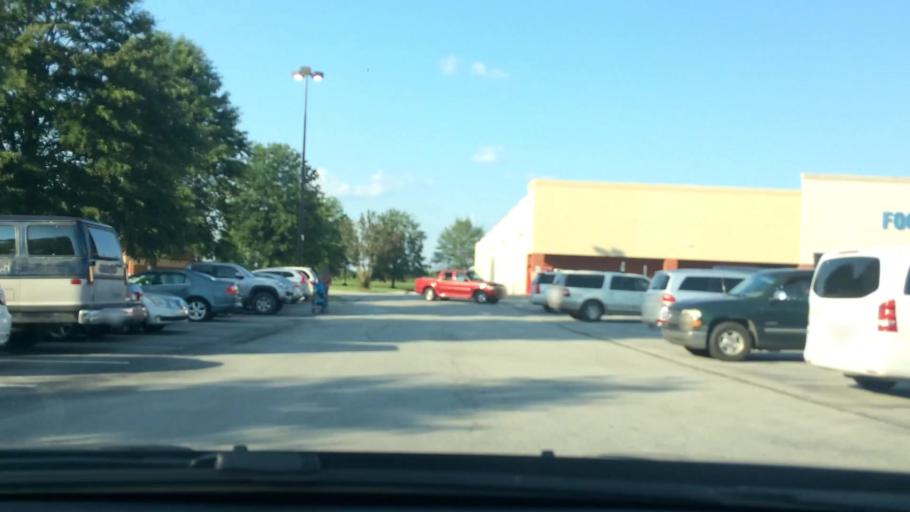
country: US
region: North Carolina
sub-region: Pitt County
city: Ayden
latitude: 35.4765
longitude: -77.4366
